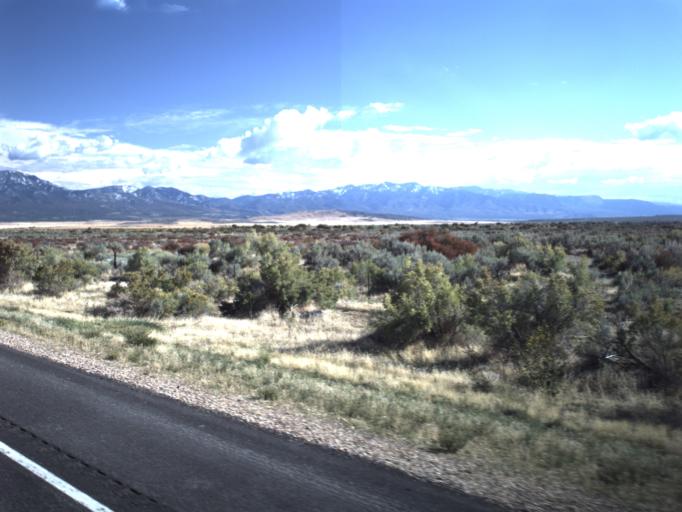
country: US
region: Utah
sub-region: Millard County
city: Fillmore
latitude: 39.1495
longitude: -112.3948
